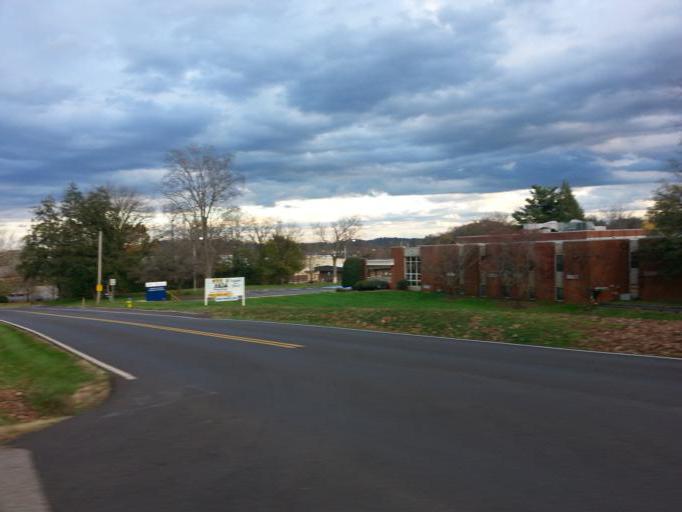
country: US
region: Tennessee
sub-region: Knox County
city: Knoxville
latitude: 35.9276
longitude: -84.0156
